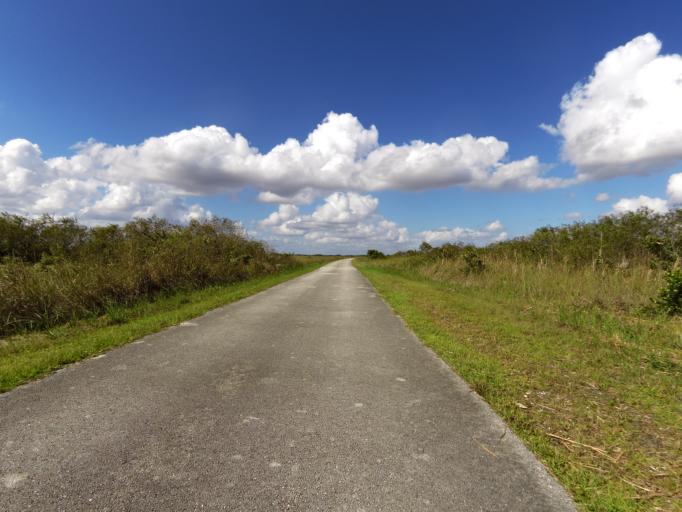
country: US
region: Florida
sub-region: Miami-Dade County
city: The Hammocks
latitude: 25.6743
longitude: -80.7620
